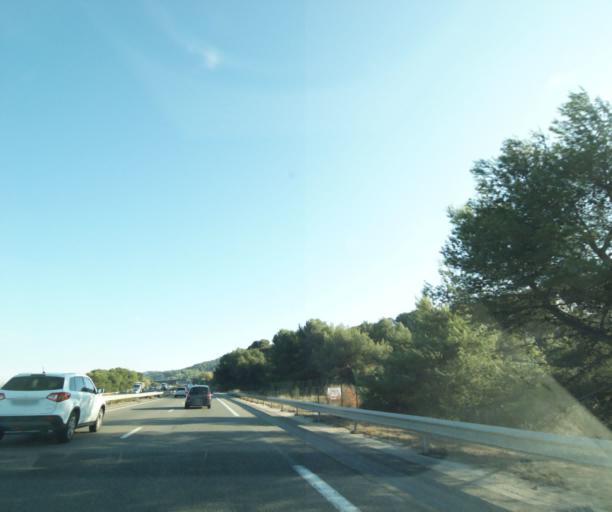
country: FR
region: Provence-Alpes-Cote d'Azur
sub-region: Departement des Bouches-du-Rhone
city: Chateauneuf-les-Martigues
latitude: 43.3980
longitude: 5.1212
